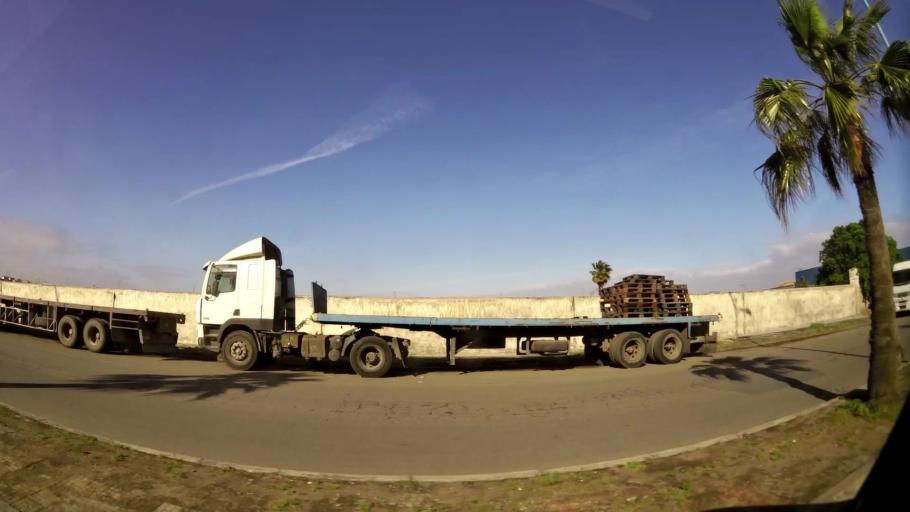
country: MA
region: Grand Casablanca
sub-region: Casablanca
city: Casablanca
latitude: 33.6005
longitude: -7.5730
